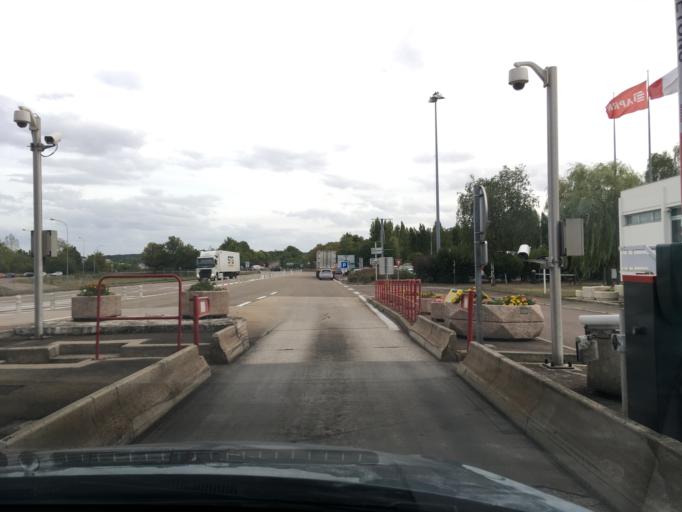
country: FR
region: Bourgogne
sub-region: Departement de l'Yonne
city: Gurgy
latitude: 47.8516
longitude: 3.5485
